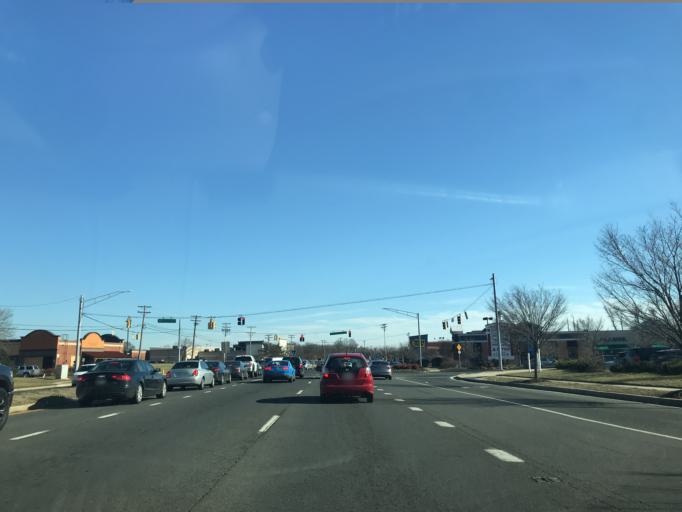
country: US
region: Maryland
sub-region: Charles County
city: Waldorf
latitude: 38.6286
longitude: -76.9149
